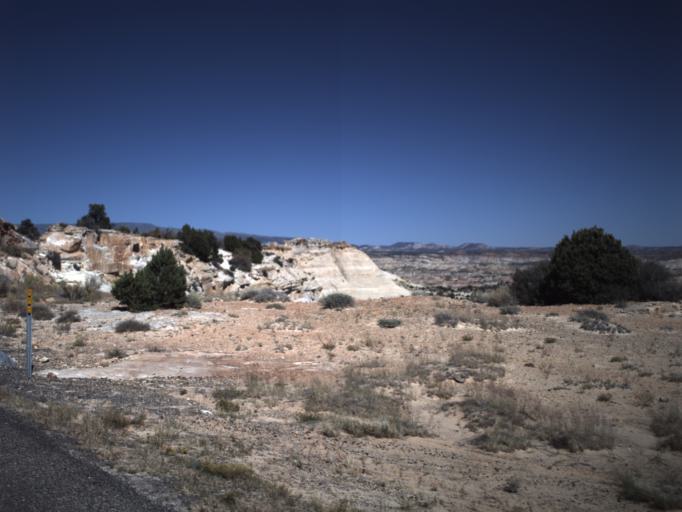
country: US
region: Utah
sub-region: Wayne County
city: Loa
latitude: 37.7442
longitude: -111.4547
